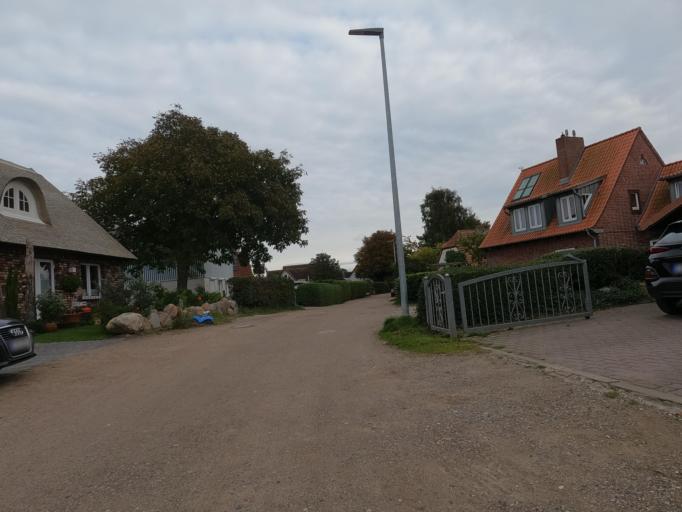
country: DE
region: Schleswig-Holstein
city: Heiligenhafen
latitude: 54.3672
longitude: 11.0210
